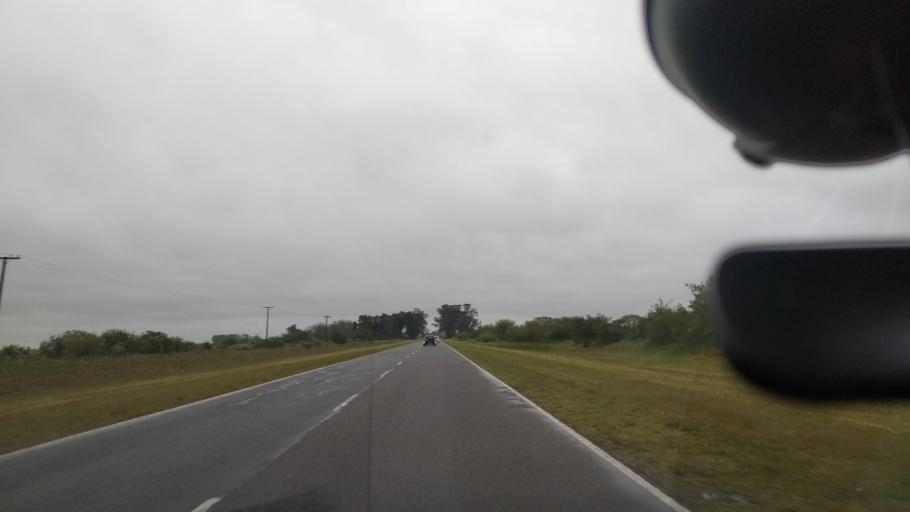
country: AR
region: Buenos Aires
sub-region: Partido de Castelli
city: Castelli
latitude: -36.0169
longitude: -57.4473
